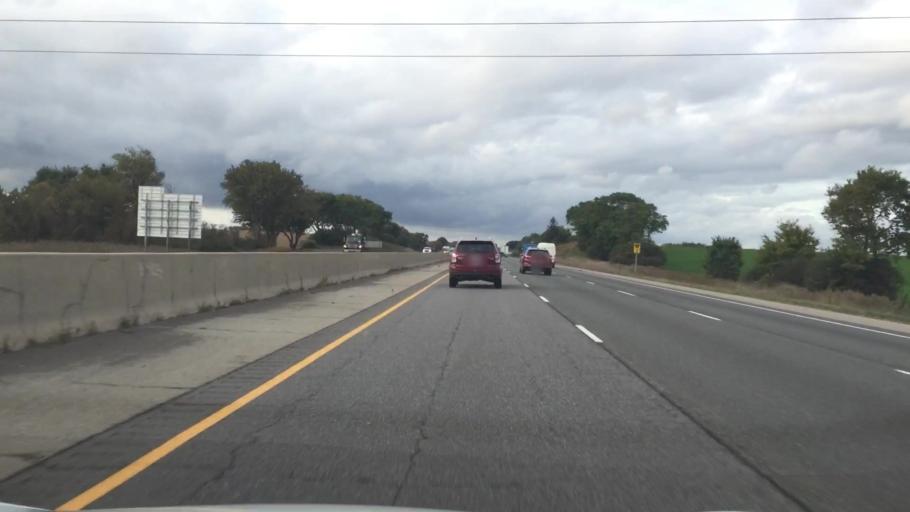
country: CA
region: Ontario
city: Ingersoll
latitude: 43.0354
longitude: -80.8431
